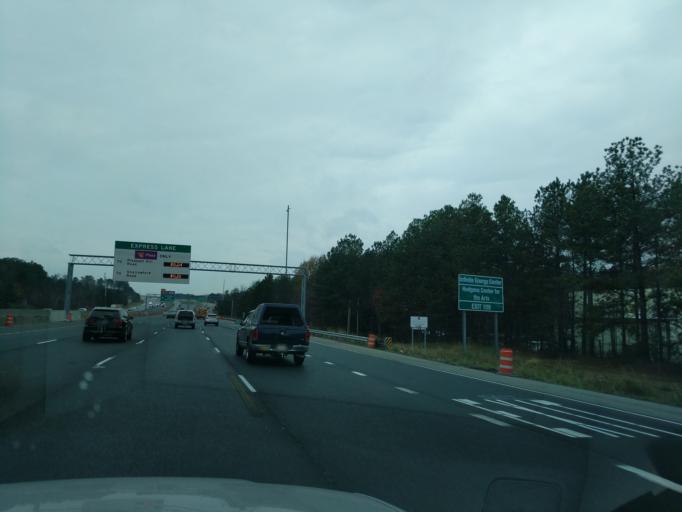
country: US
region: Georgia
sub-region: Gwinnett County
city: Suwanee
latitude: 34.0171
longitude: -84.0639
